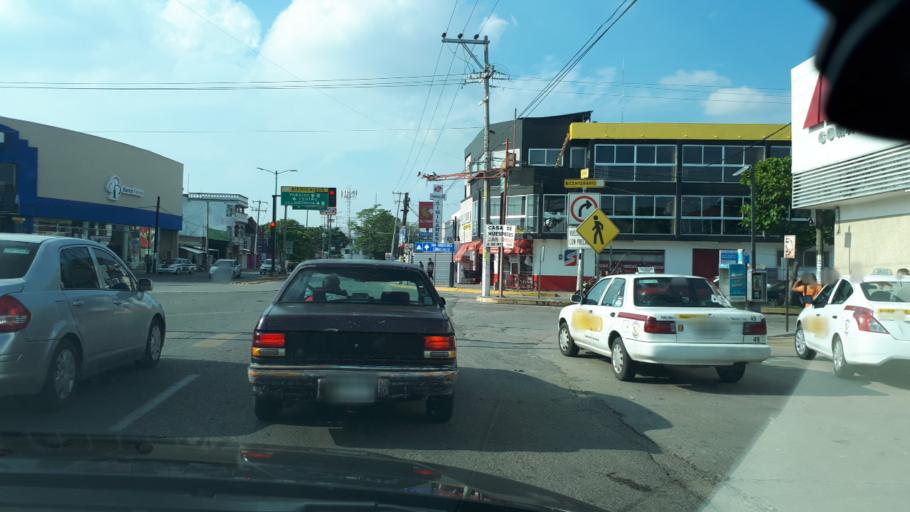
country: MX
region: Tabasco
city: Comalcalco
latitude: 18.2643
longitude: -93.2199
